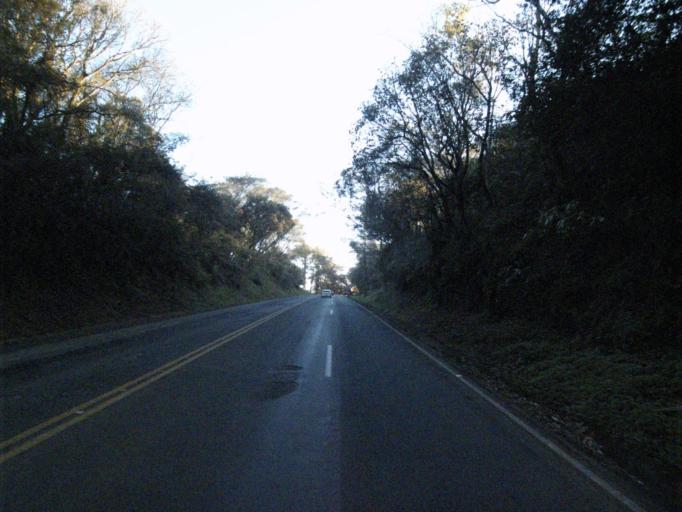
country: BR
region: Santa Catarina
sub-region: Sao Lourenco Do Oeste
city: Sao Lourenco dOeste
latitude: -26.8268
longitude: -53.0750
